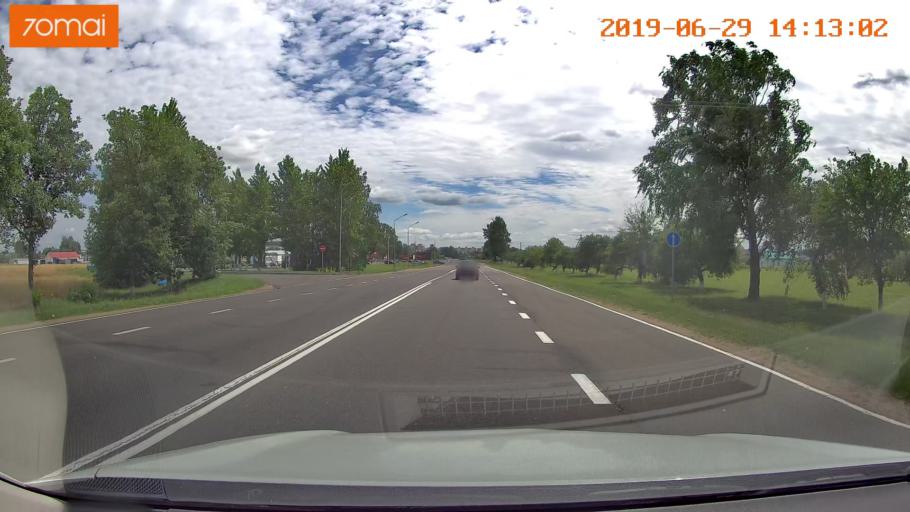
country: BY
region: Minsk
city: Salihorsk
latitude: 52.8056
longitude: 27.5096
